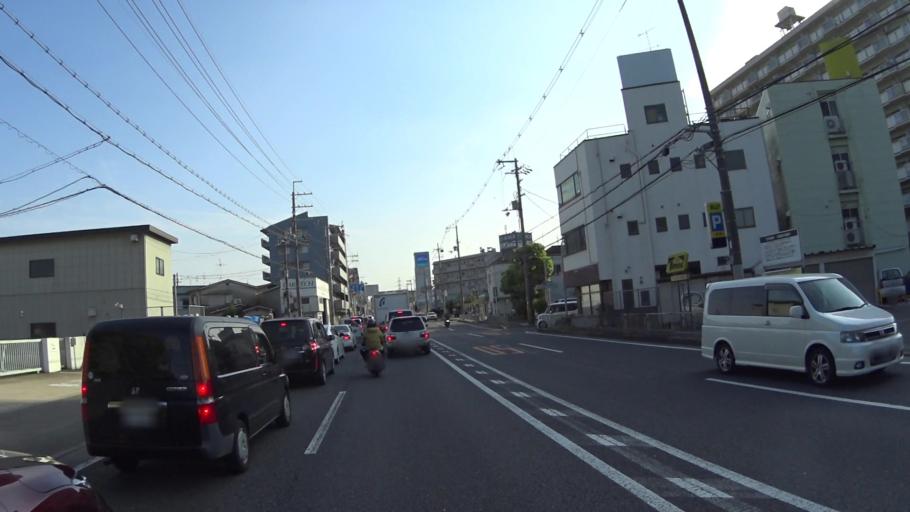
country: JP
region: Kyoto
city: Yawata
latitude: 34.8781
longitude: 135.6696
